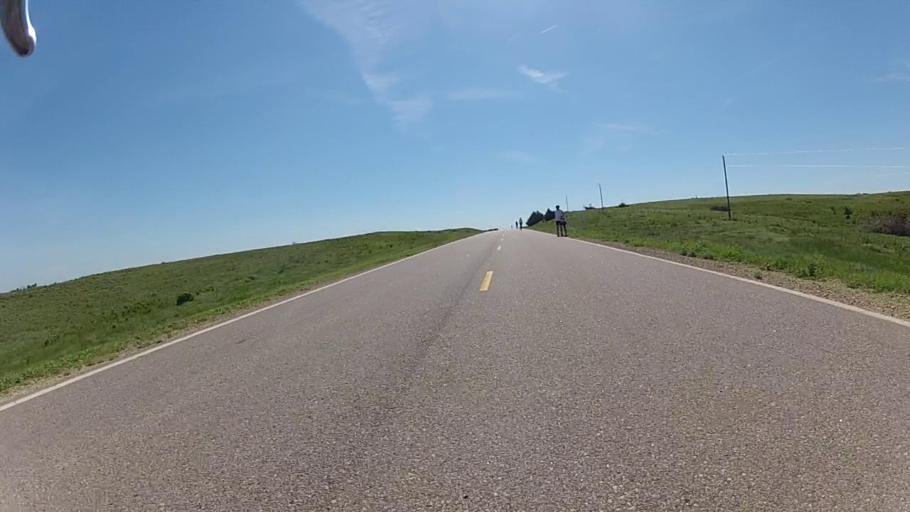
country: US
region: Kansas
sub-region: Barber County
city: Medicine Lodge
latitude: 37.2754
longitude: -98.7095
